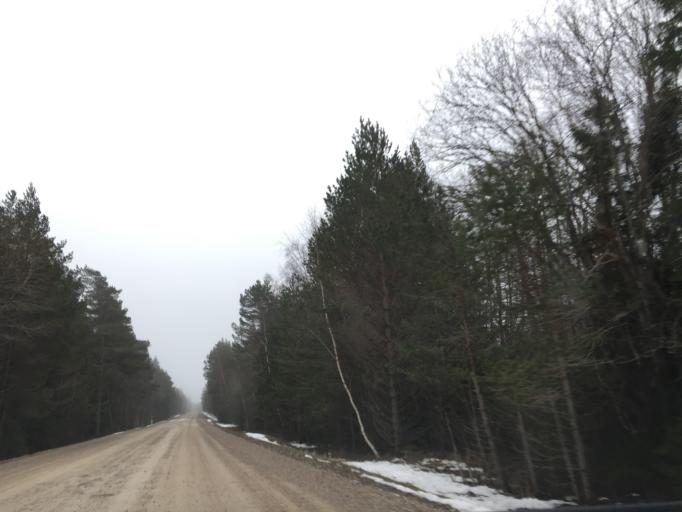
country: EE
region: Saare
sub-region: Kuressaare linn
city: Kuressaare
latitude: 58.4832
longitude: 21.9975
